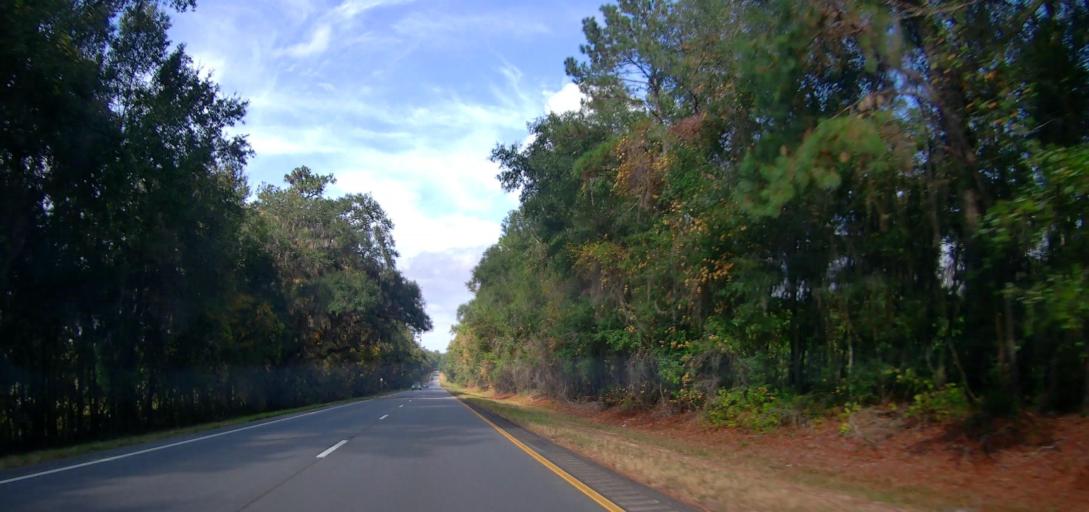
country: US
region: Georgia
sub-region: Grady County
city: Cairo
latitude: 30.6907
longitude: -84.1504
